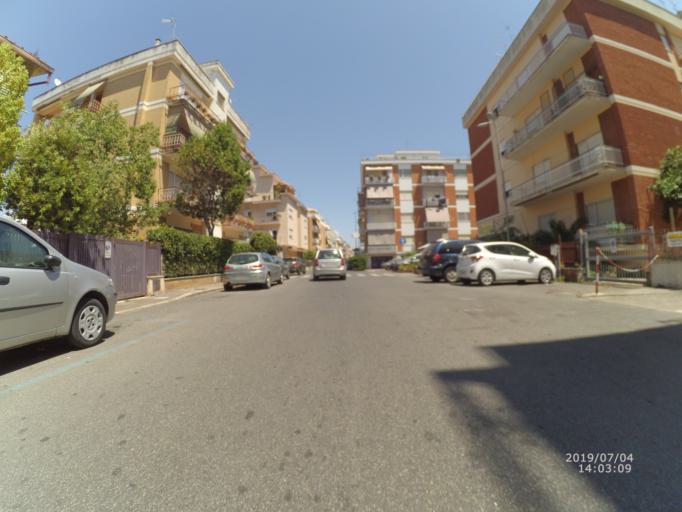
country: IT
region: Latium
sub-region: Provincia di Latina
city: Terracina
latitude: 41.2864
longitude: 13.2389
